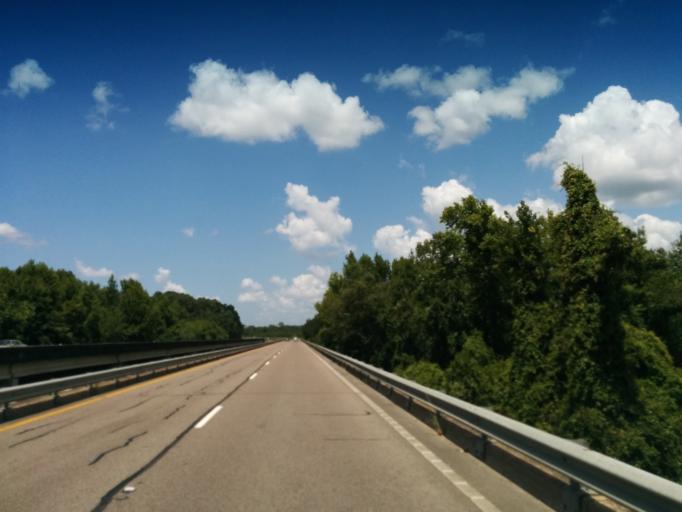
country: US
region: Texas
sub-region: Hardin County
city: Lumberton
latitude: 30.2859
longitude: -94.1916
